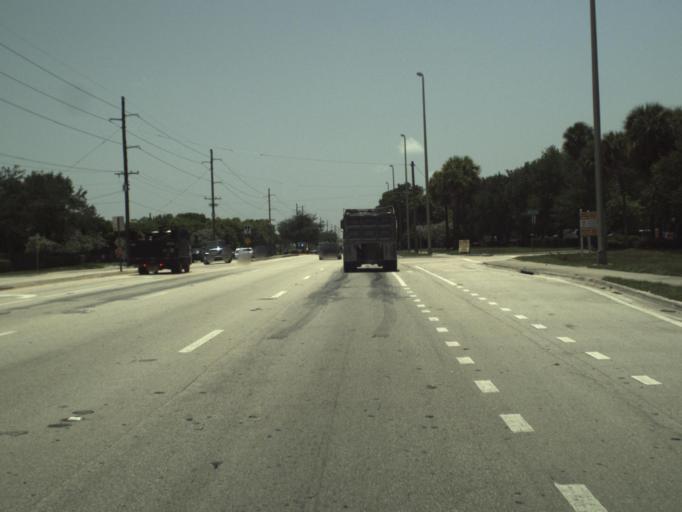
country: US
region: Florida
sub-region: Broward County
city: Coconut Creek
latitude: 26.2571
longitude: -80.1519
